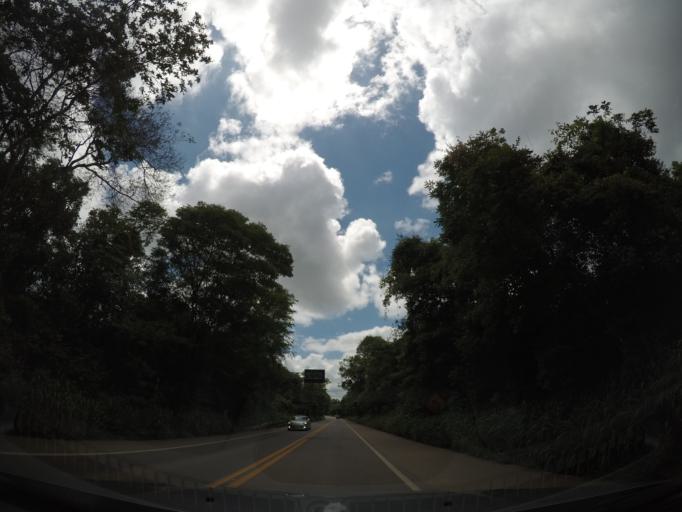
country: BR
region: Bahia
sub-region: Iraquara
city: Iraquara
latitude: -12.4791
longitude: -41.3582
